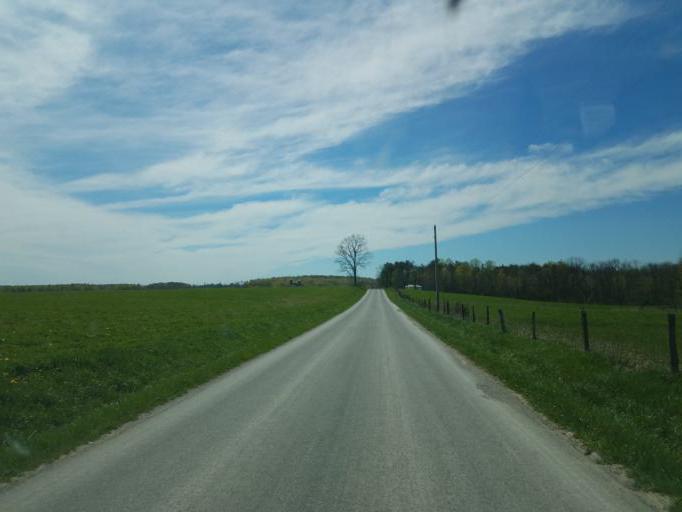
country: US
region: Ohio
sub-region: Ashland County
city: Ashland
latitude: 40.9168
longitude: -82.4271
